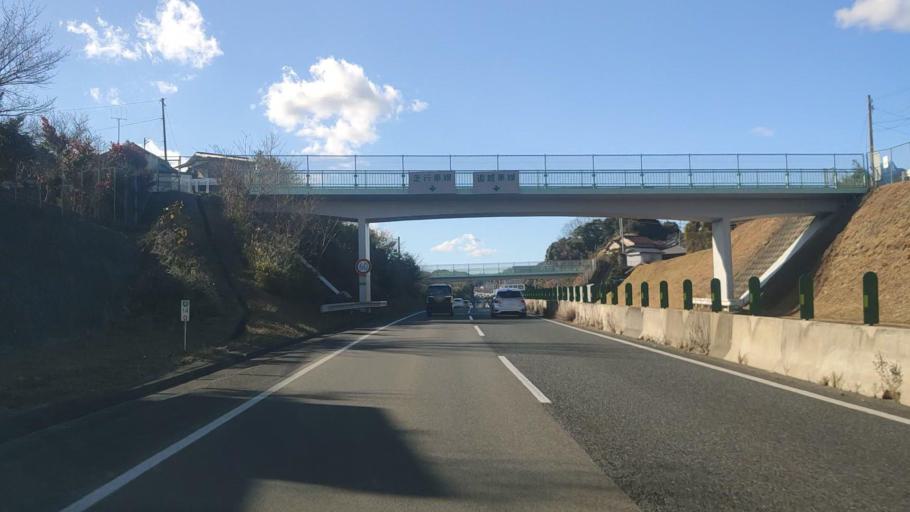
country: JP
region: Fukuoka
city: Kitakyushu
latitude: 33.8640
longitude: 130.8634
